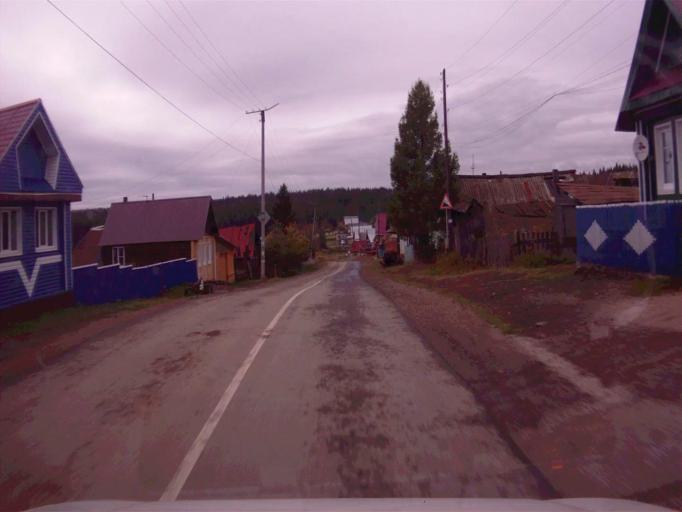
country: RU
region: Chelyabinsk
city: Nyazepetrovsk
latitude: 56.0624
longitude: 59.5746
